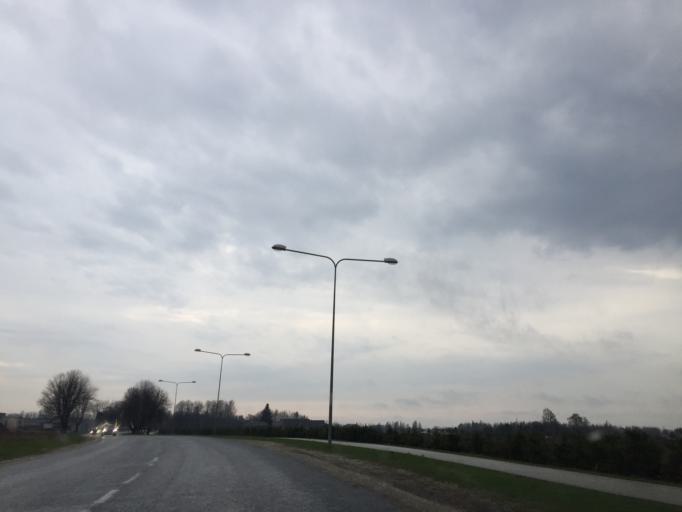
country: EE
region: Tartu
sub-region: UElenurme vald
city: Ulenurme
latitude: 58.3257
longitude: 26.7213
